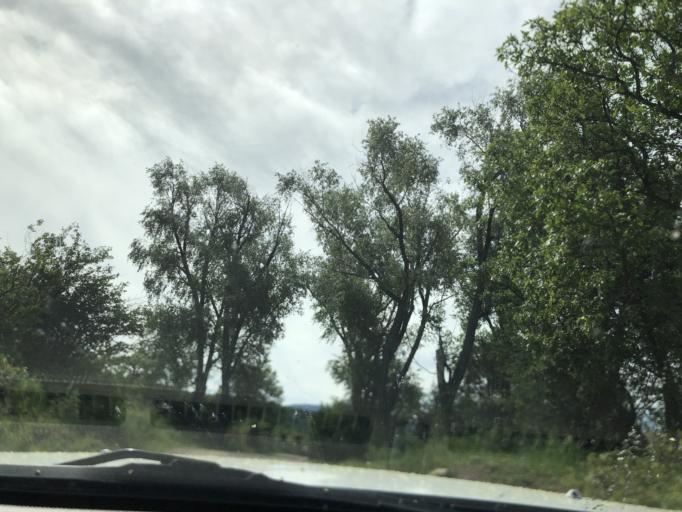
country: US
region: Colorado
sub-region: Delta County
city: Paonia
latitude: 39.0073
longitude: -107.3413
